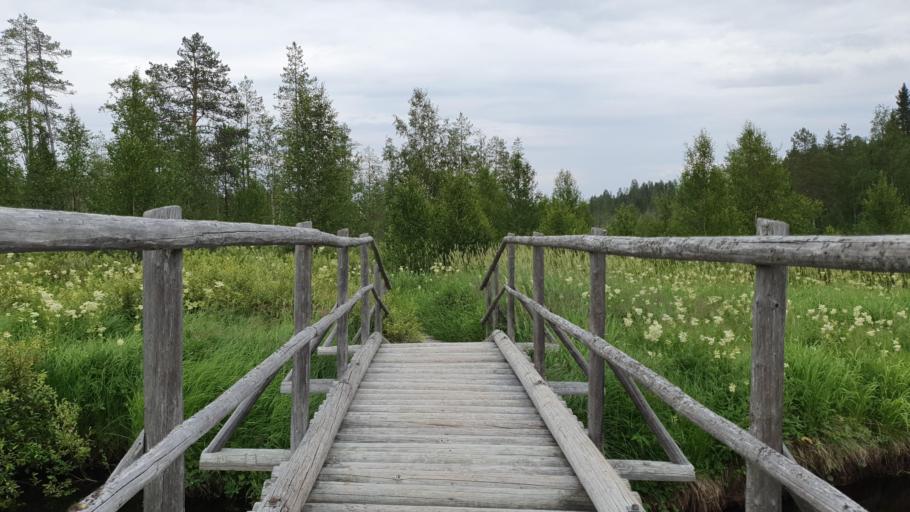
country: RU
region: Republic of Karelia
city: Kostomuksha
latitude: 64.7580
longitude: 30.0007
